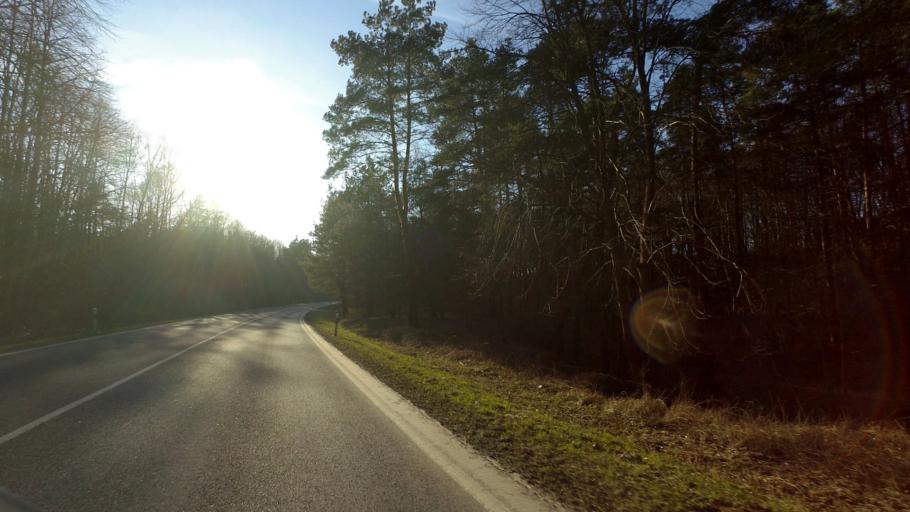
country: DE
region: Brandenburg
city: Althuttendorf
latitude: 52.9508
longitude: 13.8237
